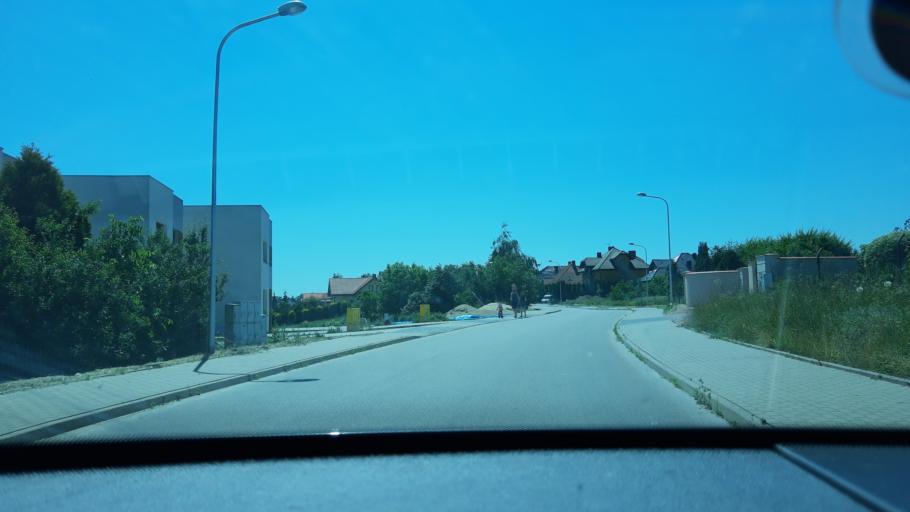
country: PL
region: Lodz Voivodeship
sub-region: Powiat sieradzki
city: Sieradz
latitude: 51.5825
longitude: 18.7402
